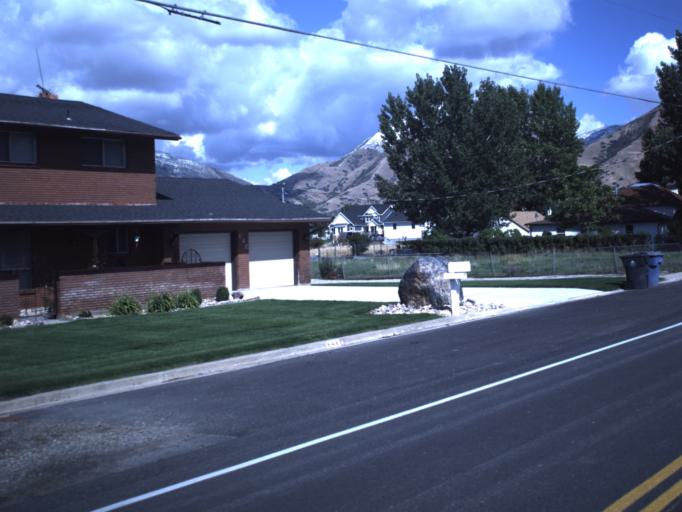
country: US
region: Utah
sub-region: Utah County
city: Mapleton
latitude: 40.1157
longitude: -111.5865
